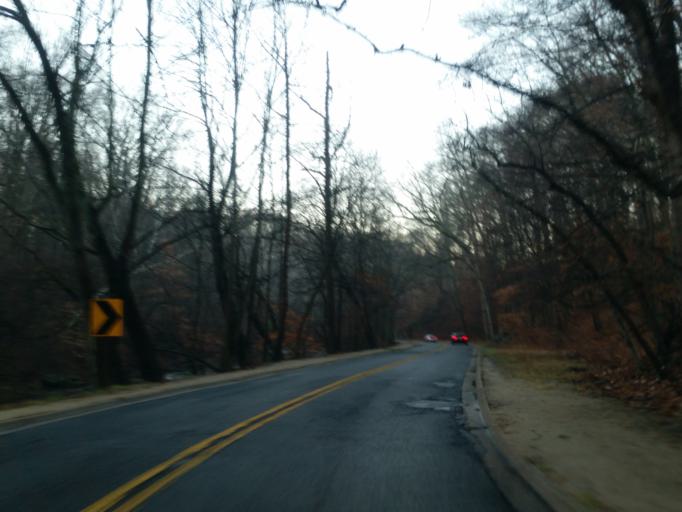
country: US
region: Maryland
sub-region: Montgomery County
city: Chevy Chase
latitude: 38.9480
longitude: -77.0443
